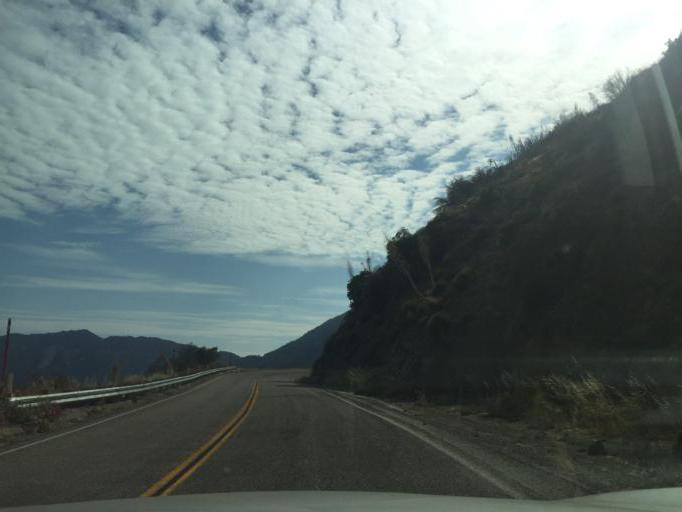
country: US
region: California
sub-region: Los Angeles County
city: Altadena
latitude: 34.2683
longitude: -118.0800
